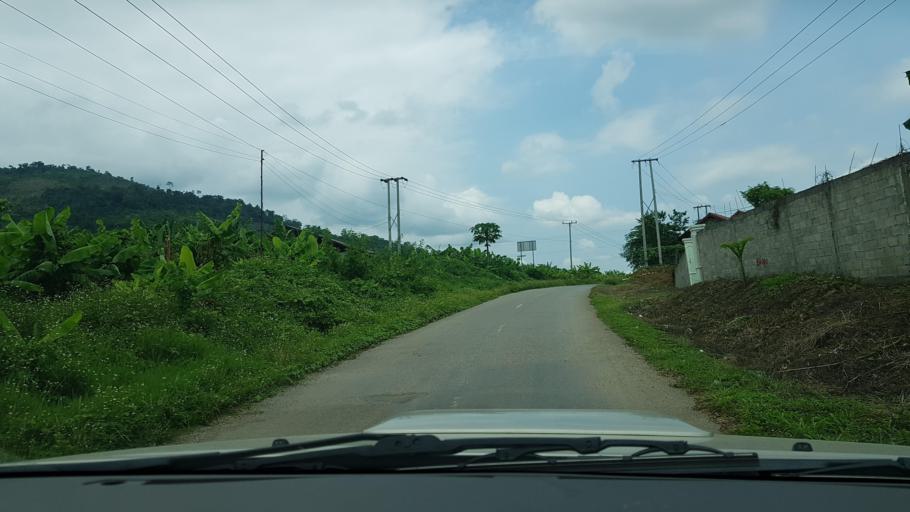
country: TH
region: Nan
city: Chaloem Phra Kiat
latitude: 19.9989
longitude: 101.2851
